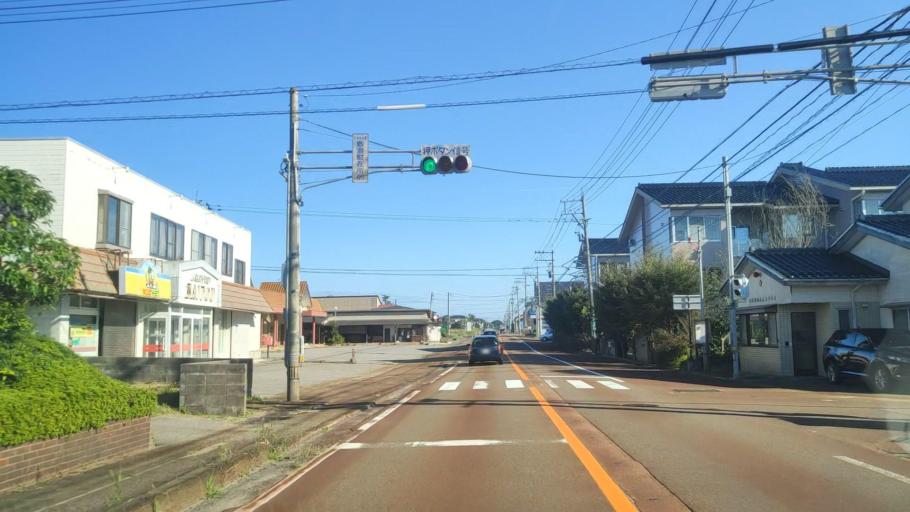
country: JP
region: Ishikawa
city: Hakui
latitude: 36.8519
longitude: 136.7692
